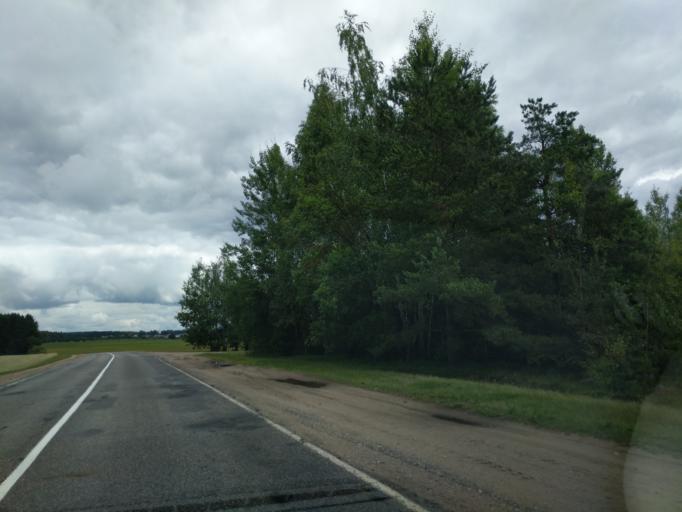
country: BY
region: Minsk
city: Il'ya
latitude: 54.5537
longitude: 27.2129
